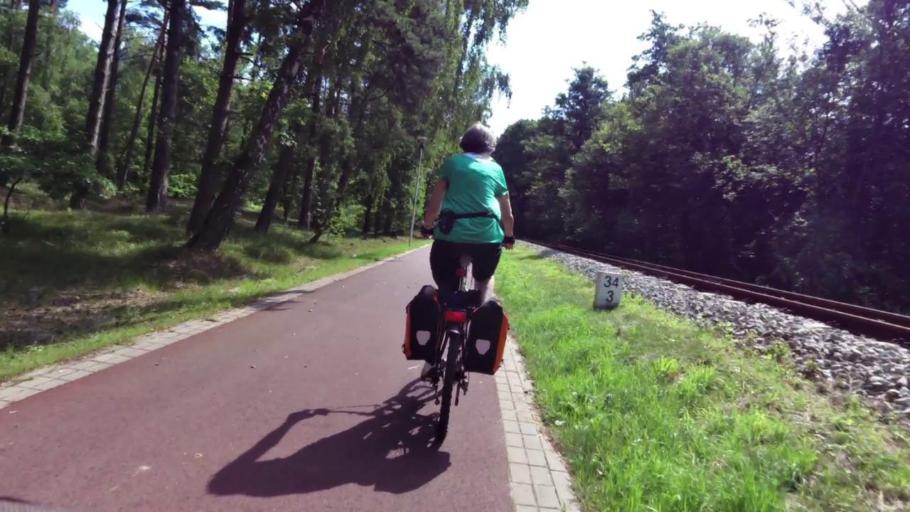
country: PL
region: West Pomeranian Voivodeship
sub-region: Powiat gryficki
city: Karnice
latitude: 54.0944
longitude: 15.1081
